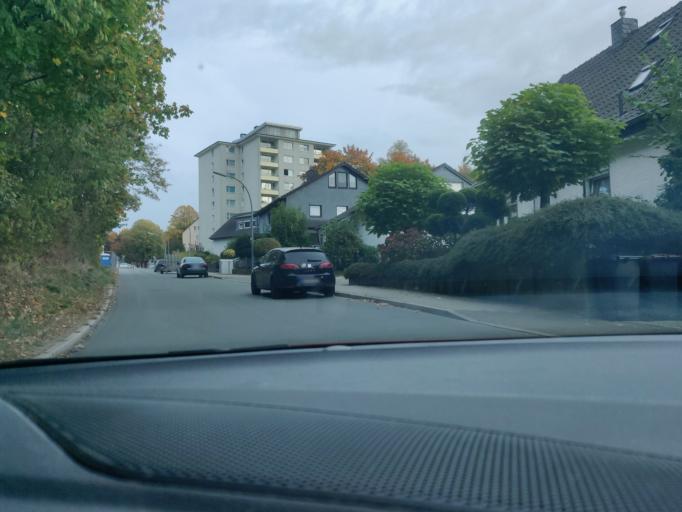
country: DE
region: North Rhine-Westphalia
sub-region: Regierungsbezirk Dusseldorf
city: Velbert
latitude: 51.3407
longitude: 7.0081
